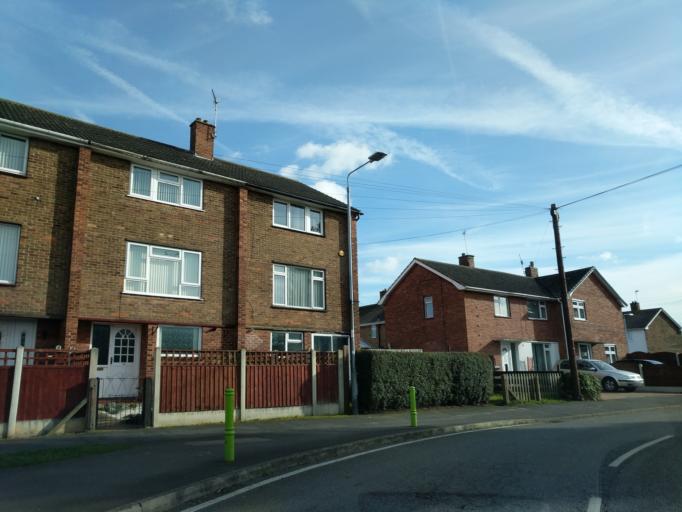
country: GB
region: England
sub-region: Nottinghamshire
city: Cotgrave
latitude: 52.9097
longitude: -1.0350
